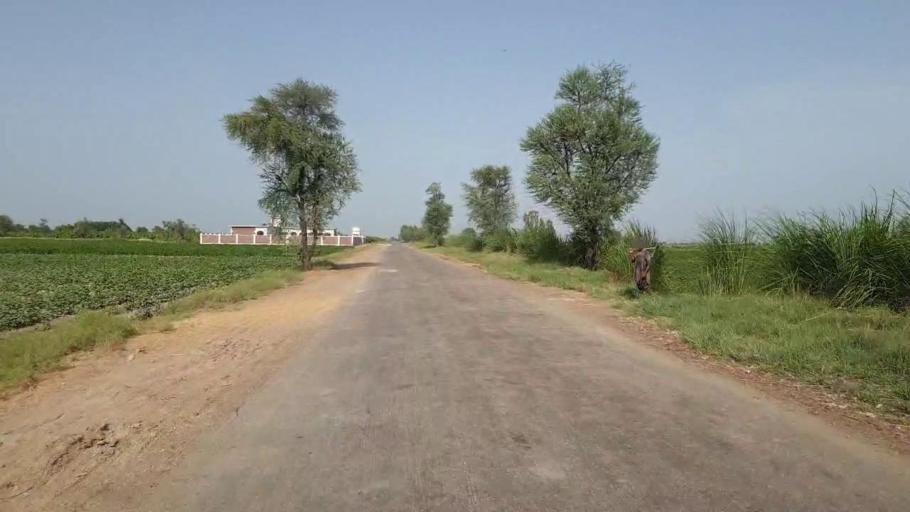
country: PK
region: Sindh
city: Sakrand
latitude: 26.2847
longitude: 68.2344
